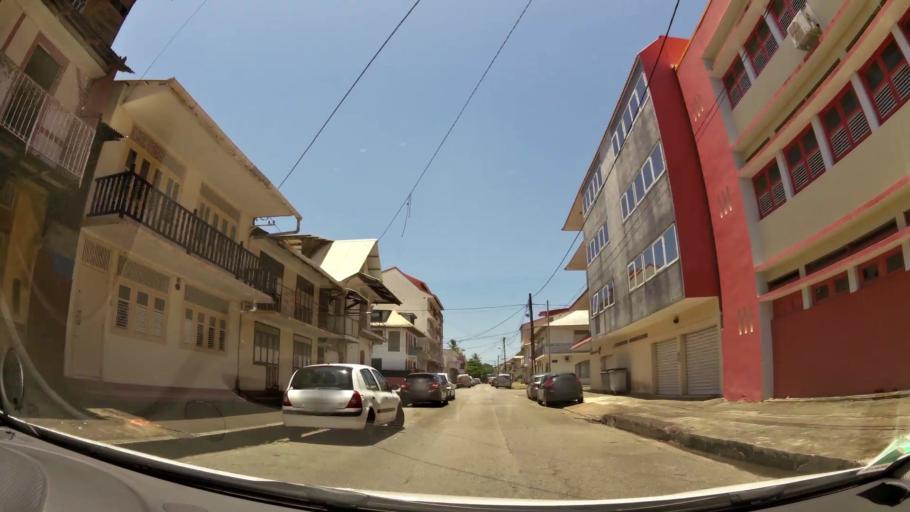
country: GF
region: Guyane
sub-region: Guyane
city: Cayenne
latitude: 4.9425
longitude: -52.3306
